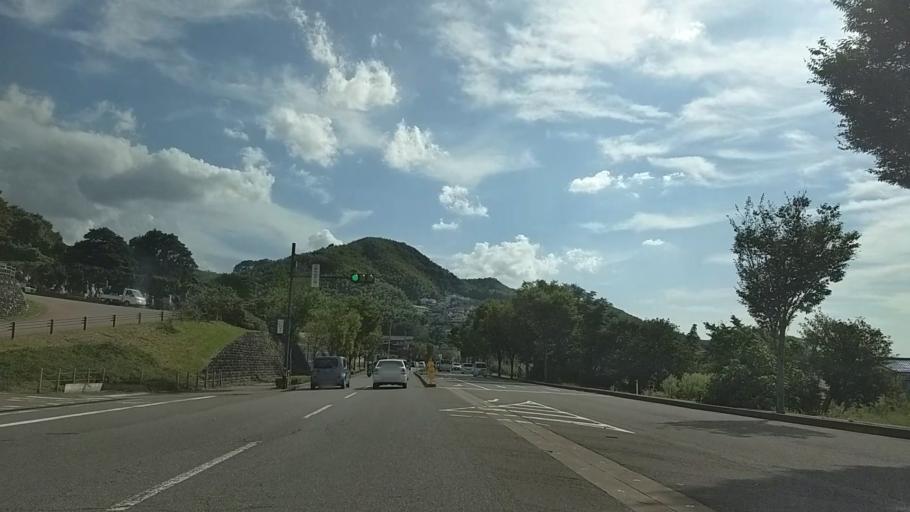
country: JP
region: Ishikawa
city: Nonoichi
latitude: 36.5306
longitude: 136.6527
